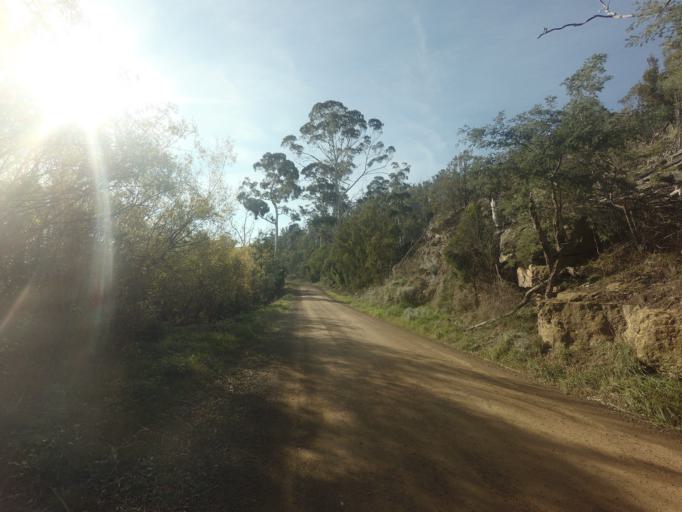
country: AU
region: Tasmania
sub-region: Brighton
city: Bridgewater
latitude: -42.5219
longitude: 147.4154
